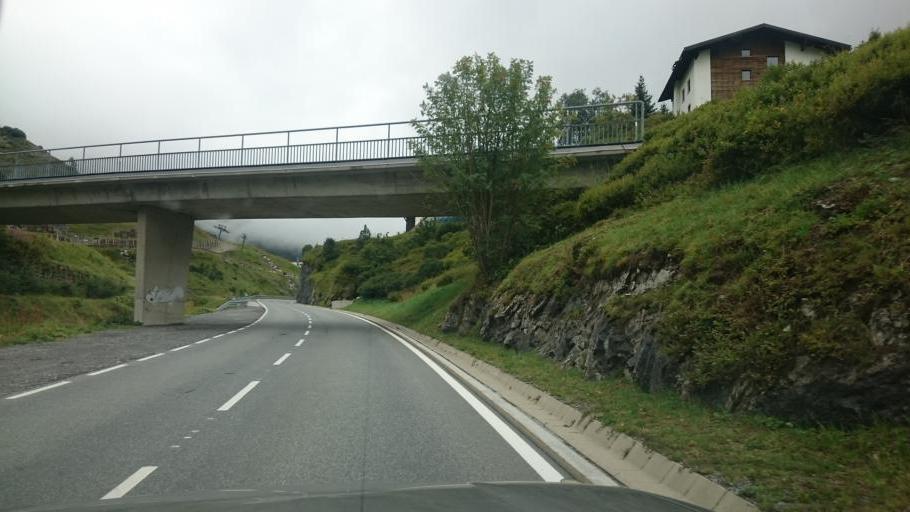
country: AT
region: Vorarlberg
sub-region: Politischer Bezirk Bludenz
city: Lech
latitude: 47.1754
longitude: 10.1621
